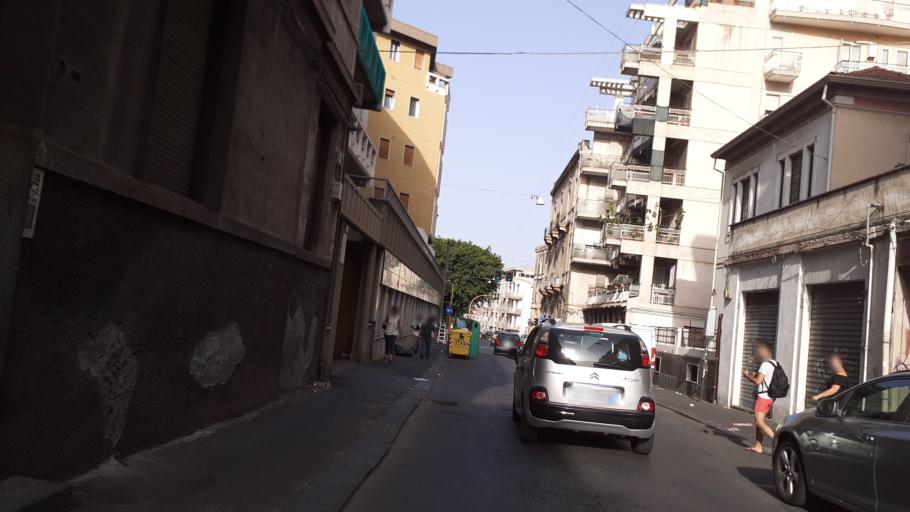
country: IT
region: Sicily
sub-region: Catania
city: Catania
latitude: 37.5088
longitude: 15.0814
